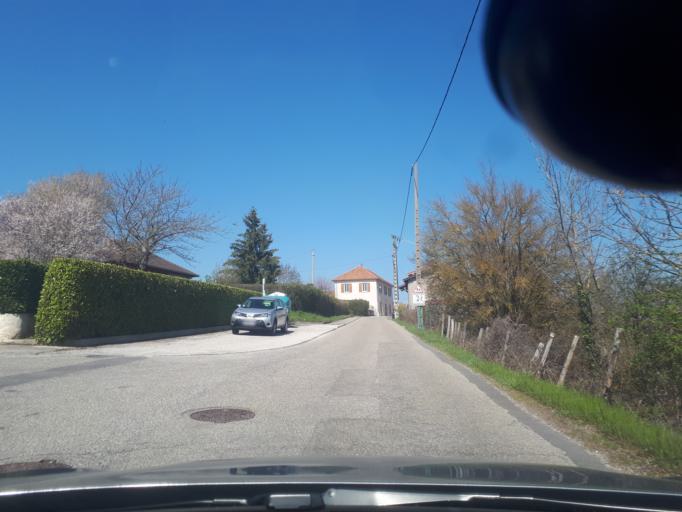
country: FR
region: Rhone-Alpes
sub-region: Departement de l'Isere
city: Nivolas-Vermelle
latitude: 45.5270
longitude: 5.3391
